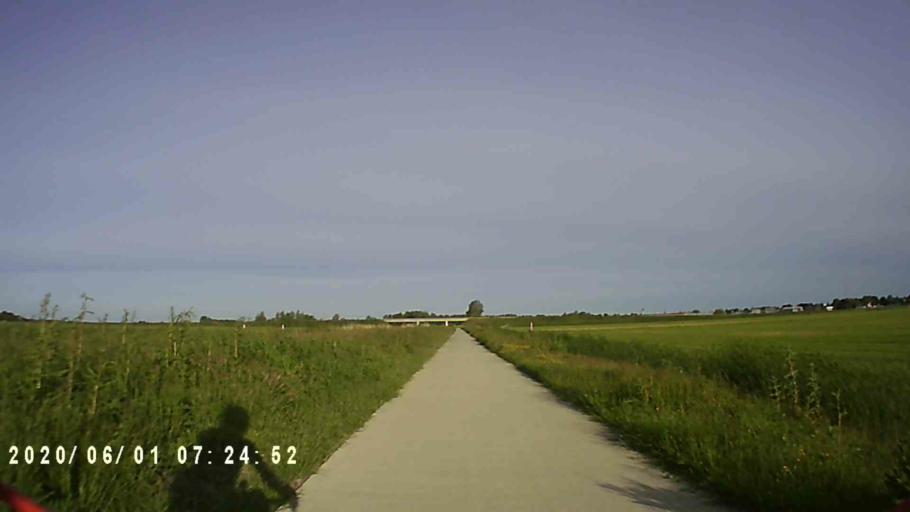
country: NL
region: Friesland
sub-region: Gemeente Dantumadiel
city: Walterswald
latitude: 53.3174
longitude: 6.0275
